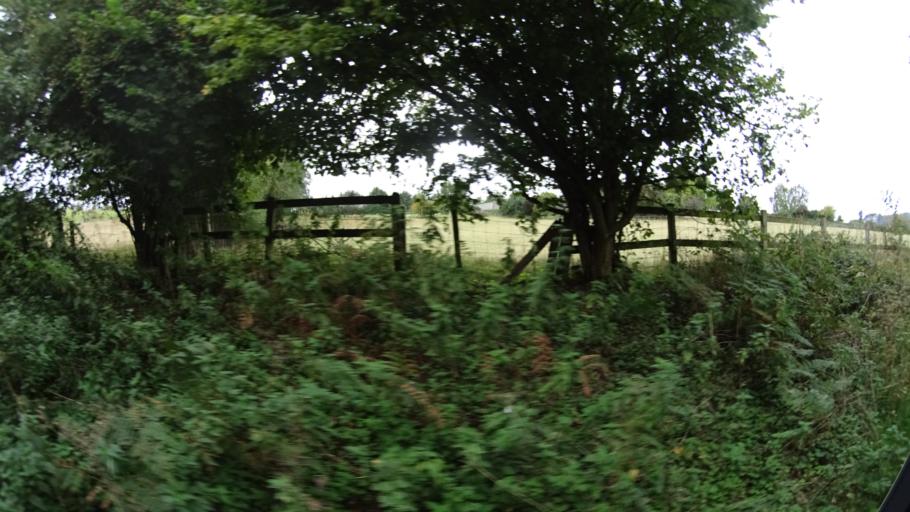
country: GB
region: England
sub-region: Hampshire
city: Long Sutton
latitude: 51.2038
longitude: -0.8952
